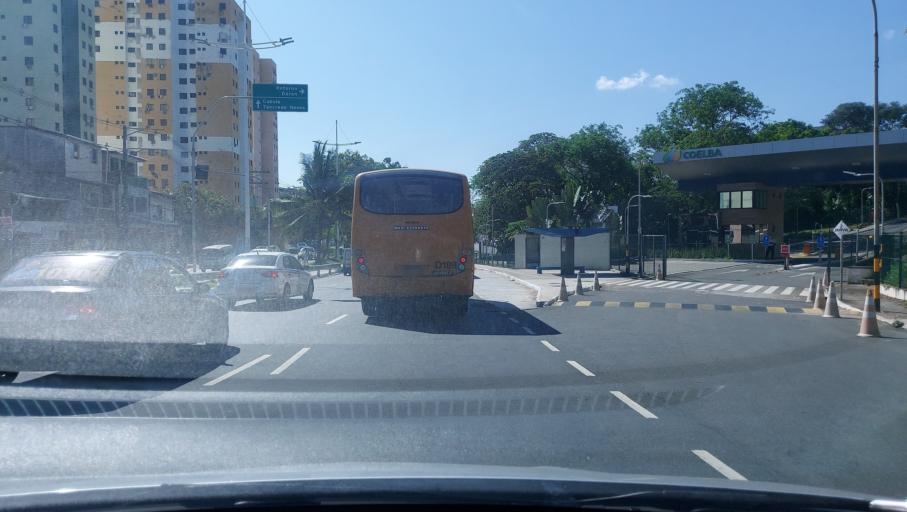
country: BR
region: Bahia
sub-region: Salvador
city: Salvador
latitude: -12.9622
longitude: -38.4372
